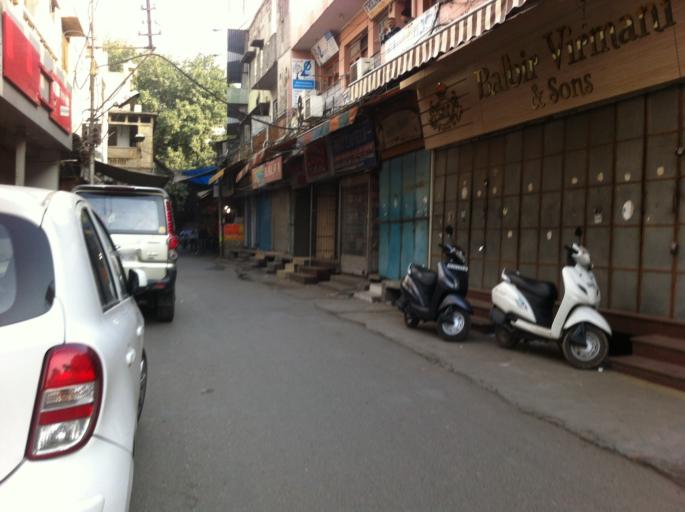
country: IN
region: Punjab
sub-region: Kapurthala
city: Phagwara
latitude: 31.2214
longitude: 75.7721
